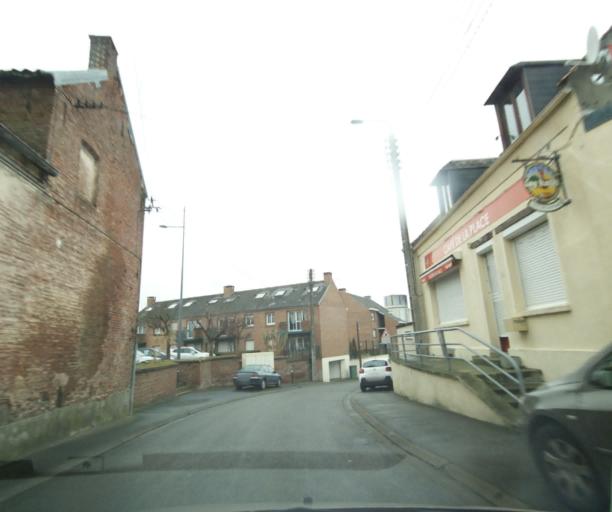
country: FR
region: Nord-Pas-de-Calais
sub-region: Departement du Nord
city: Prouvy
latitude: 50.3191
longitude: 3.4491
